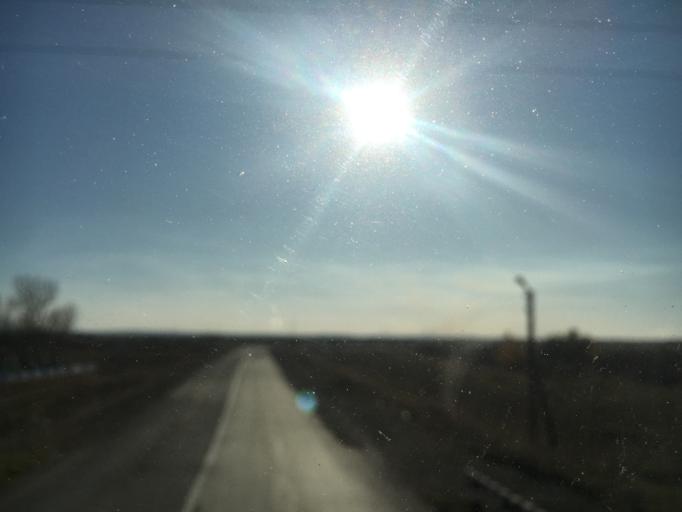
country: KZ
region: Qaraghandy
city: Tokarevka
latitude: 50.1214
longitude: 73.2136
